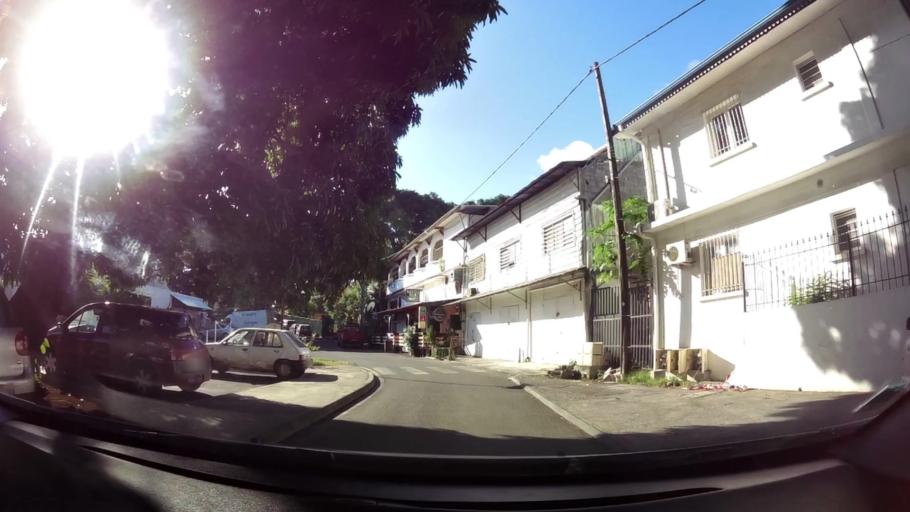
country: YT
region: Dzaoudzi
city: Dzaoudzi
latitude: -12.7816
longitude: 45.2564
